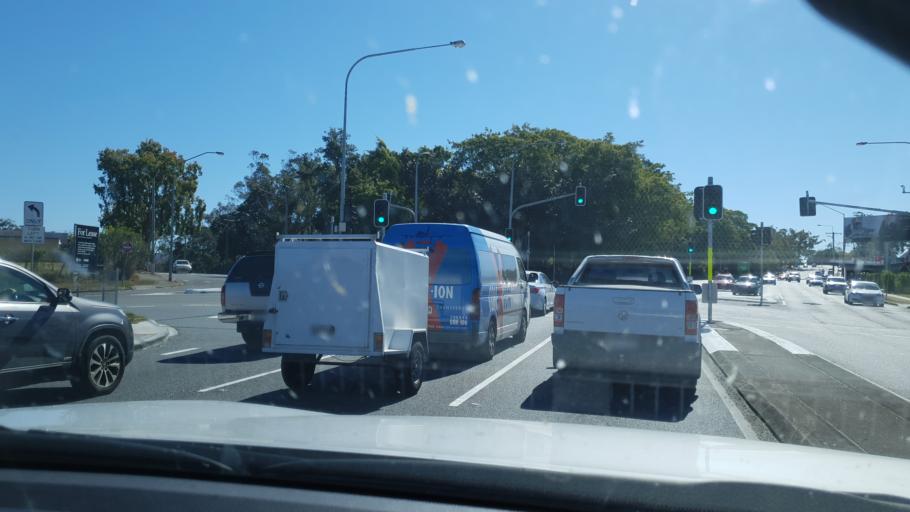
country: AU
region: Queensland
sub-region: Brisbane
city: Annerley
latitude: -27.5003
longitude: 153.0287
